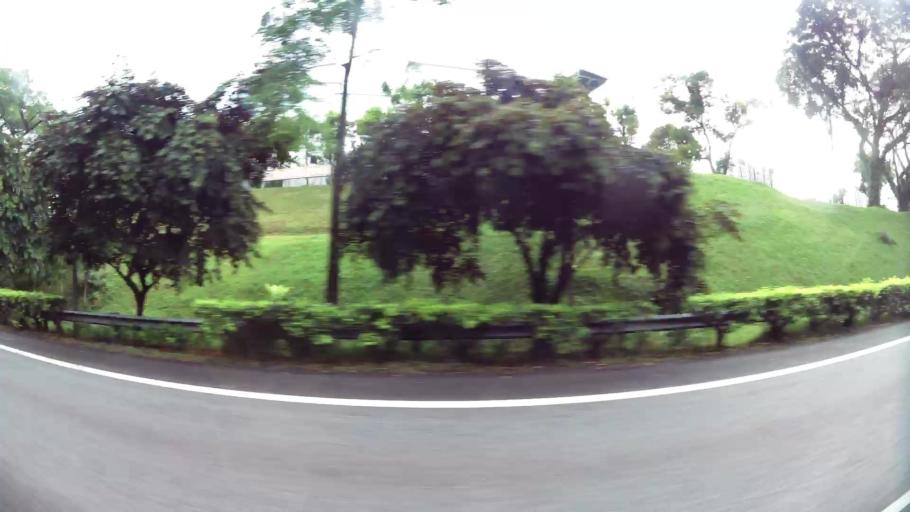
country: SG
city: Singapore
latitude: 1.2825
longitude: 103.8140
